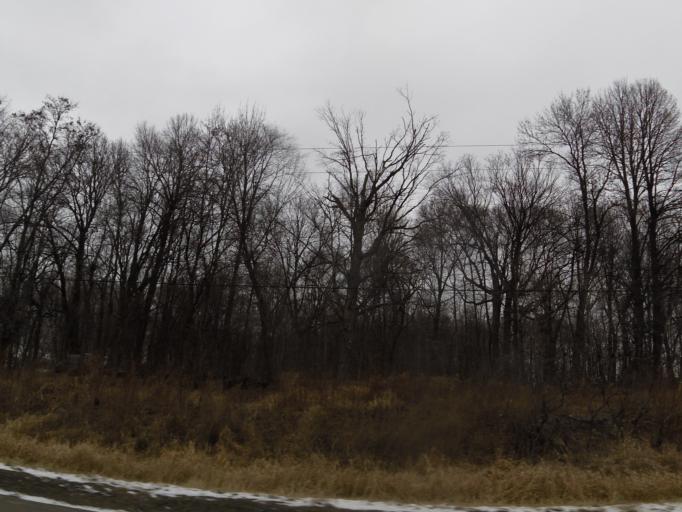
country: US
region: Minnesota
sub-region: Wright County
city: Delano
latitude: 45.0633
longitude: -93.8100
